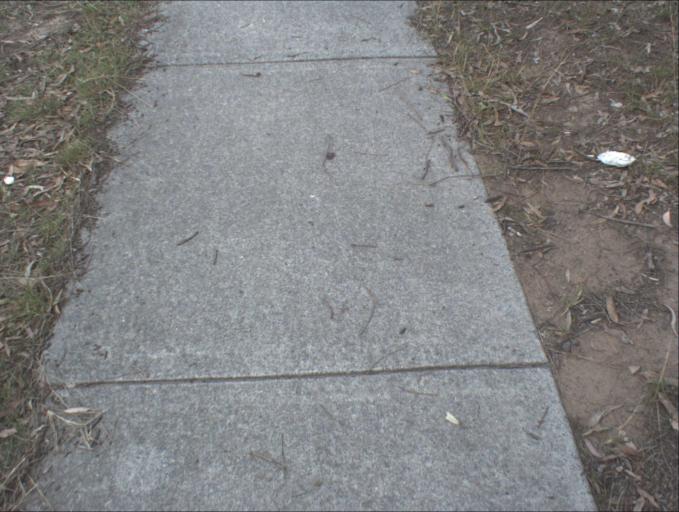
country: AU
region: Queensland
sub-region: Logan
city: Waterford West
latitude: -27.6930
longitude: 153.1525
